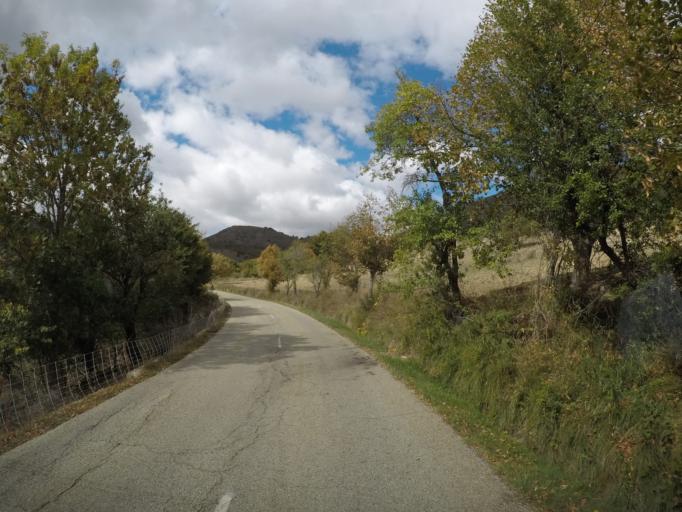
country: FR
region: Provence-Alpes-Cote d'Azur
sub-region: Departement du Vaucluse
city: Sault
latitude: 44.1835
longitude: 5.5175
